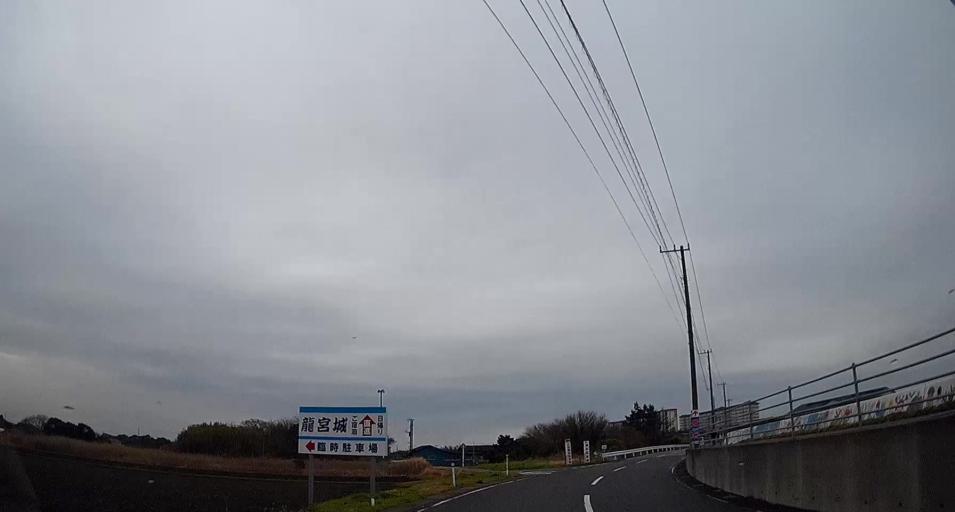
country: JP
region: Chiba
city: Kisarazu
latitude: 35.4254
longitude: 139.9021
